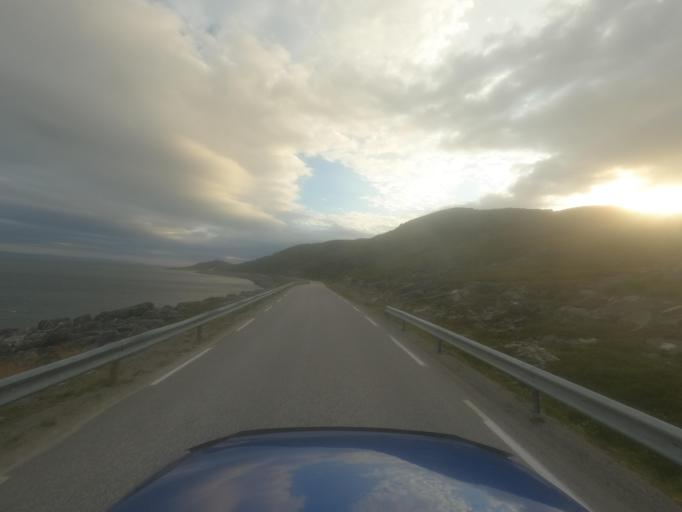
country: NO
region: Finnmark Fylke
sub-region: Nordkapp
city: Honningsvag
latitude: 70.7064
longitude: 25.5226
